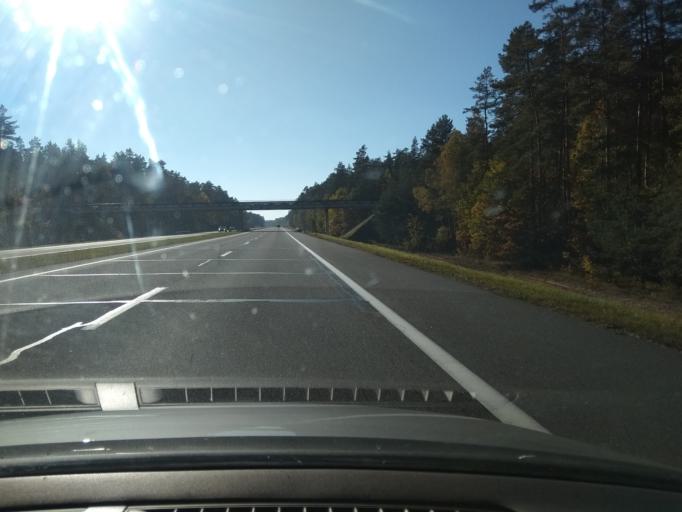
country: BY
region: Brest
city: Baranovichi
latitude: 53.0359
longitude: 25.8155
